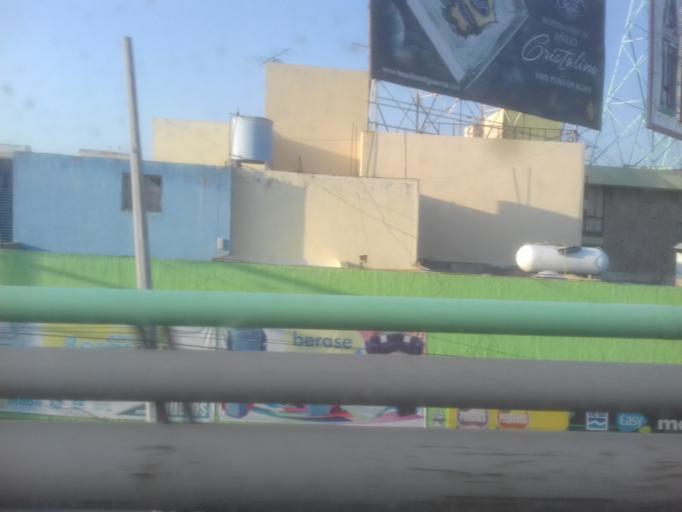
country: MX
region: Aguascalientes
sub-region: Aguascalientes
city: Aguascalientes
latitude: 21.8653
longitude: -102.2937
